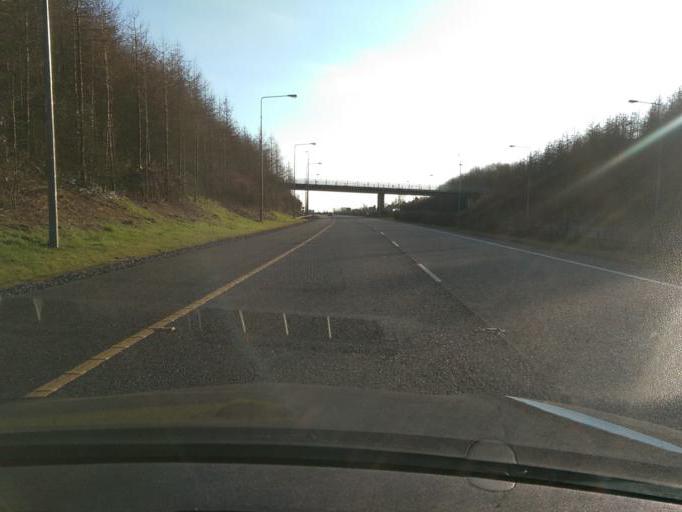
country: IE
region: Leinster
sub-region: Laois
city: Portlaoise
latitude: 53.0512
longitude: -7.2382
